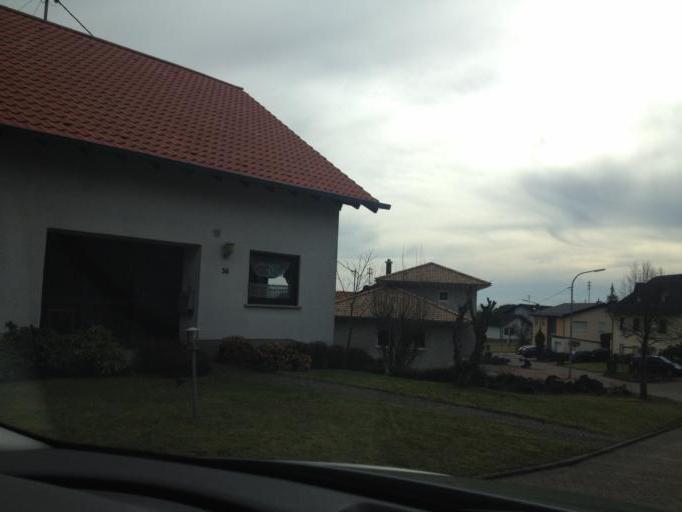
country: DE
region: Saarland
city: Oberthal
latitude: 49.5162
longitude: 7.0672
